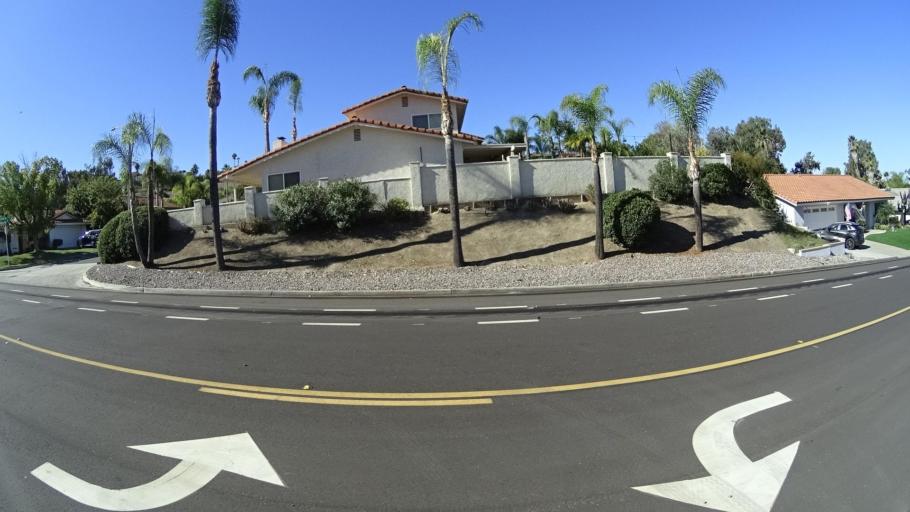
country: US
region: California
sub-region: San Diego County
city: Bonita
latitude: 32.6649
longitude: -117.0018
